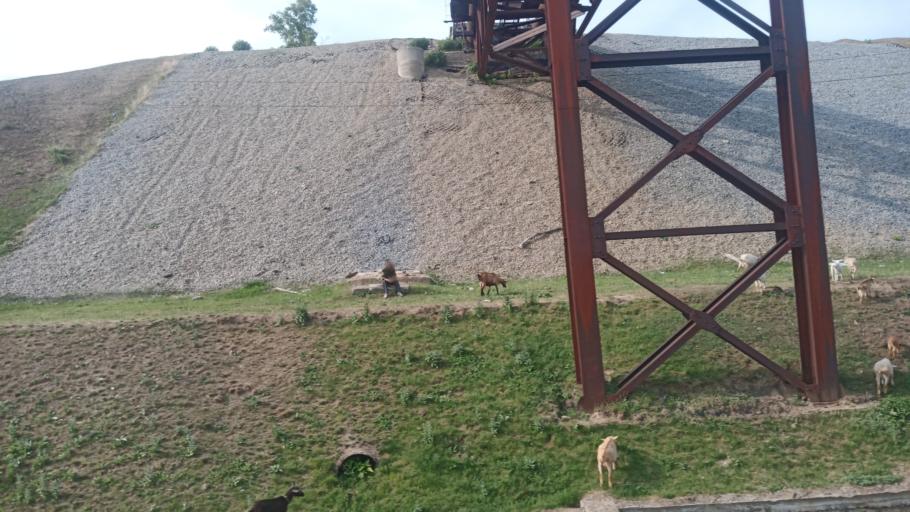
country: RU
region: Altai Krai
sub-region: Gorod Barnaulskiy
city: Barnaul
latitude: 53.3736
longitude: 83.7970
